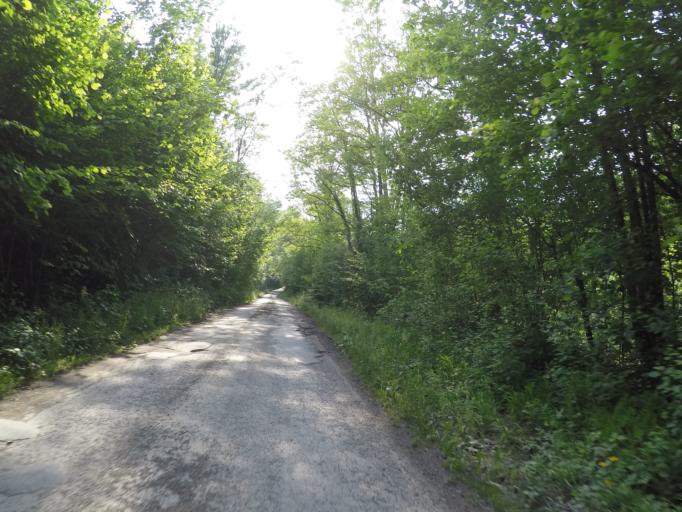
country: BE
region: Wallonia
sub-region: Province de Namur
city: Assesse
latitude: 50.3281
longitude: 4.9949
